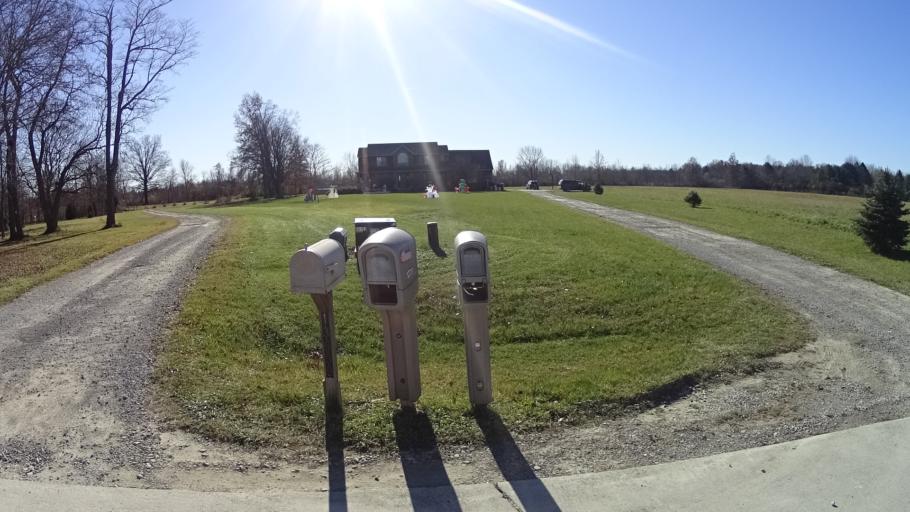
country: US
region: Ohio
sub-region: Lorain County
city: Oberlin
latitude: 41.2925
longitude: -82.1624
